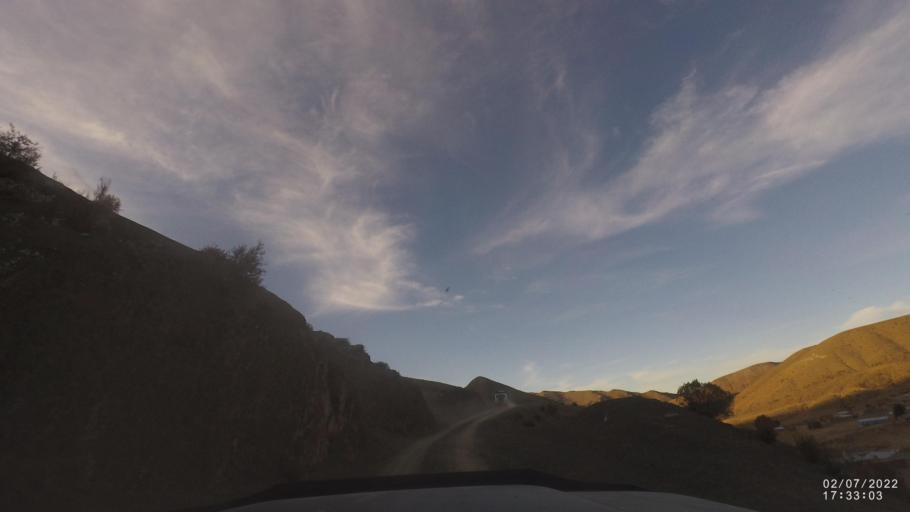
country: BO
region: Cochabamba
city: Irpa Irpa
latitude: -17.8844
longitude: -66.6188
